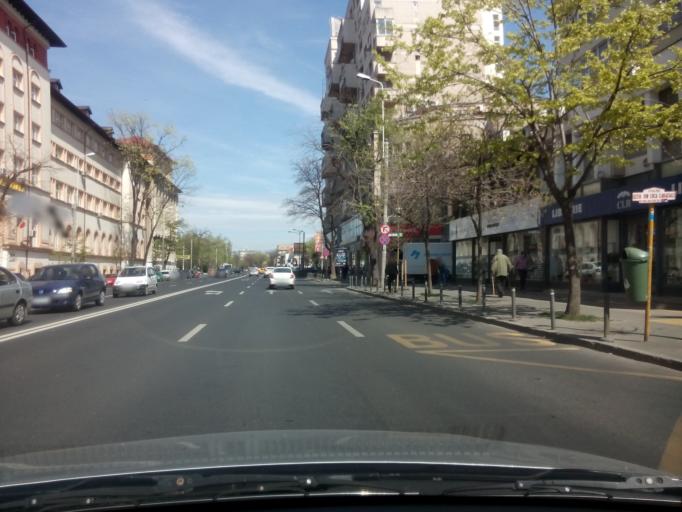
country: RO
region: Bucuresti
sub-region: Municipiul Bucuresti
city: Bucharest
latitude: 44.4581
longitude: 26.0957
